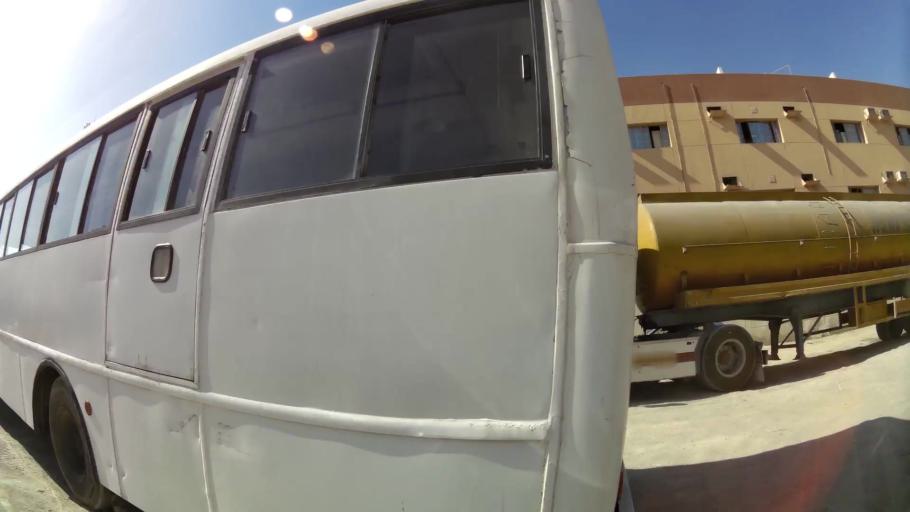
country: AE
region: Dubai
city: Dubai
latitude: 25.0089
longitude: 55.1051
